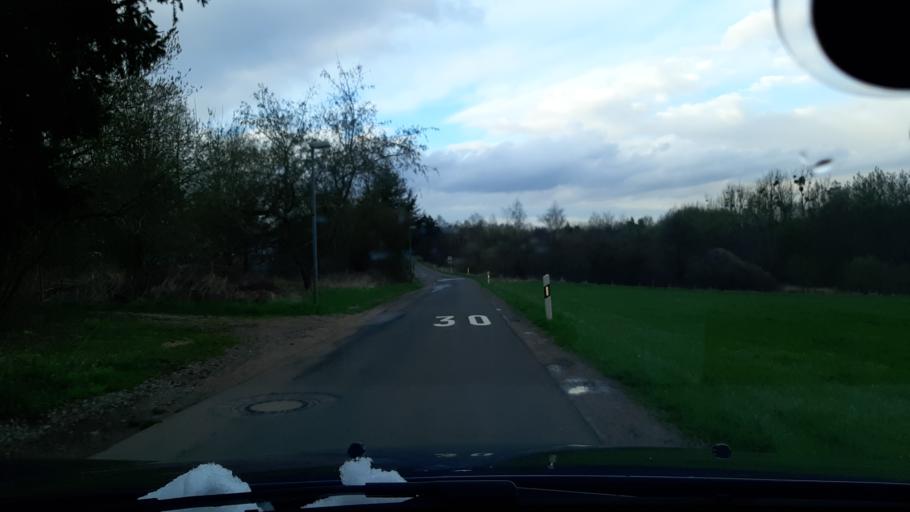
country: DE
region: North Rhine-Westphalia
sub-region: Regierungsbezirk Koln
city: Mechernich
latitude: 50.6053
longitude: 6.6844
